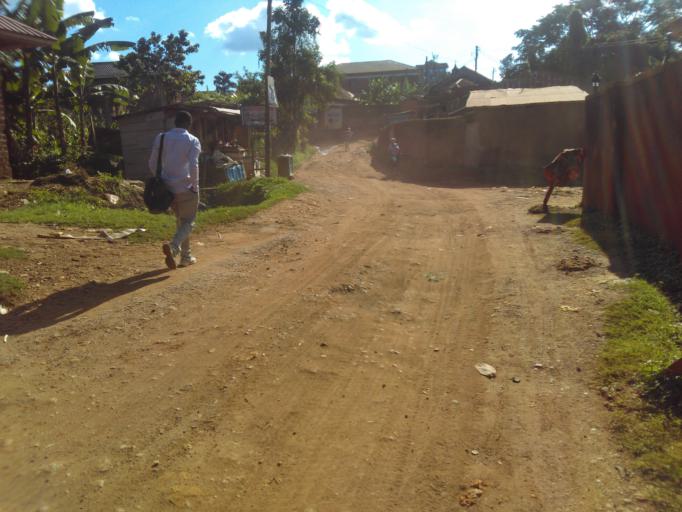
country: UG
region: Central Region
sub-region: Wakiso District
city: Entebbe
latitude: -0.2529
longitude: 32.5647
